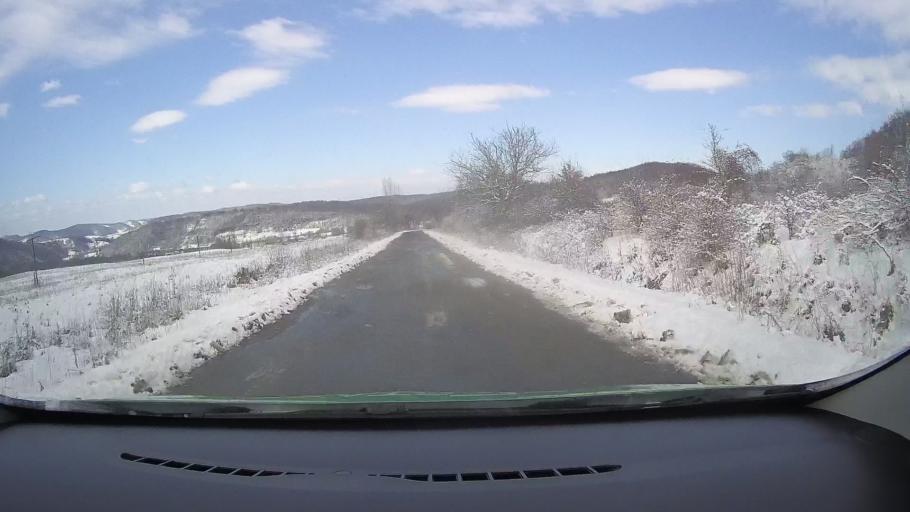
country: RO
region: Sibiu
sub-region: Comuna Mihaileni
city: Mihaileni
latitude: 46.0053
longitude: 24.4255
